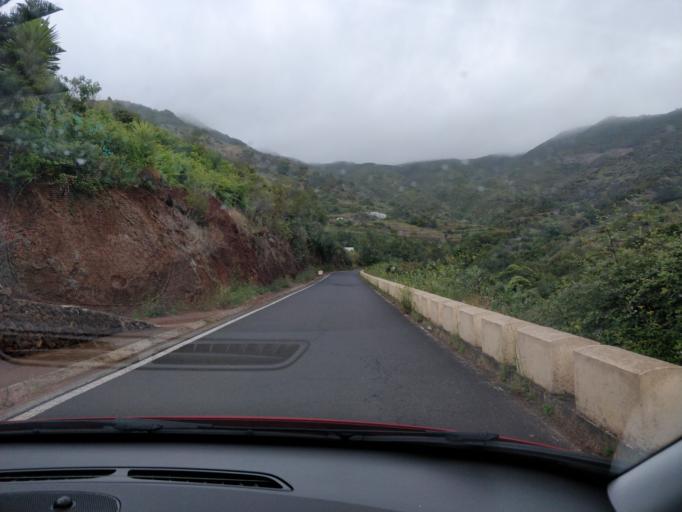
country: ES
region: Canary Islands
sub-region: Provincia de Santa Cruz de Tenerife
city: Santiago del Teide
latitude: 28.3251
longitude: -16.8452
